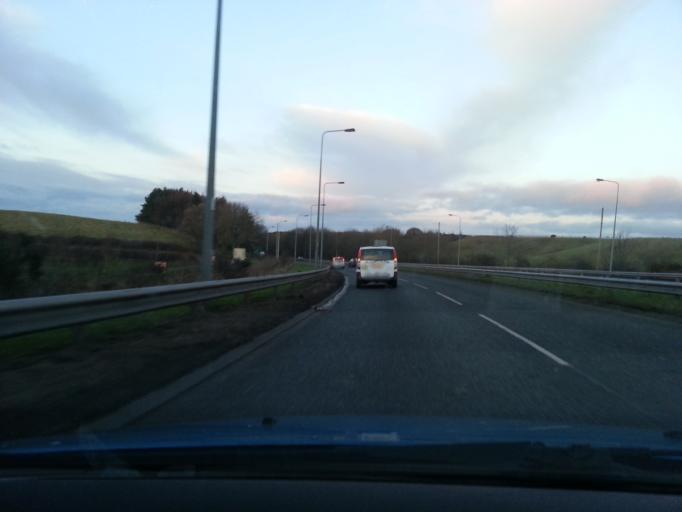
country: GB
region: England
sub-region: County Durham
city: Durham
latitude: 54.8070
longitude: -1.5888
